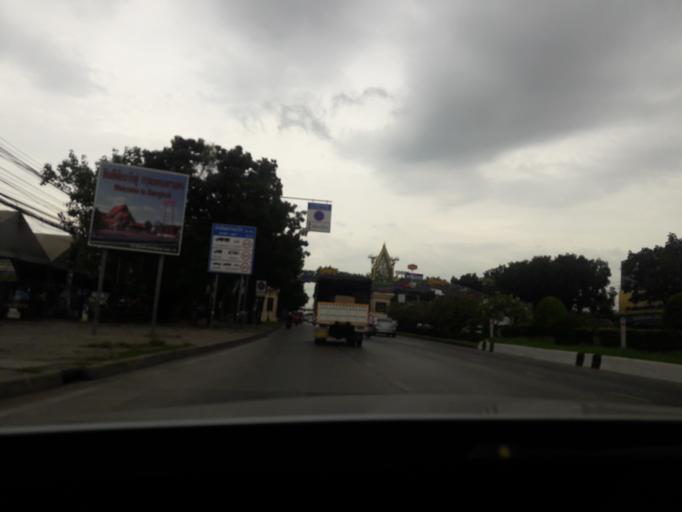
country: TH
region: Bangkok
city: Nong Khaem
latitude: 13.7047
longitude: 100.3322
